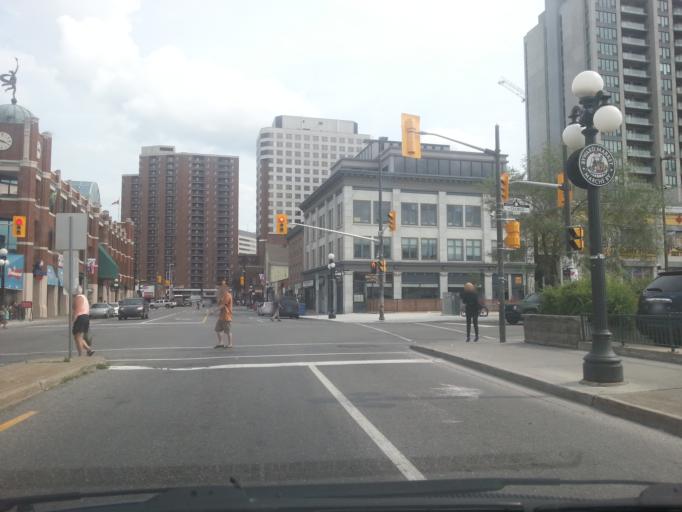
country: CA
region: Ontario
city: Ottawa
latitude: 45.4281
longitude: -75.6905
